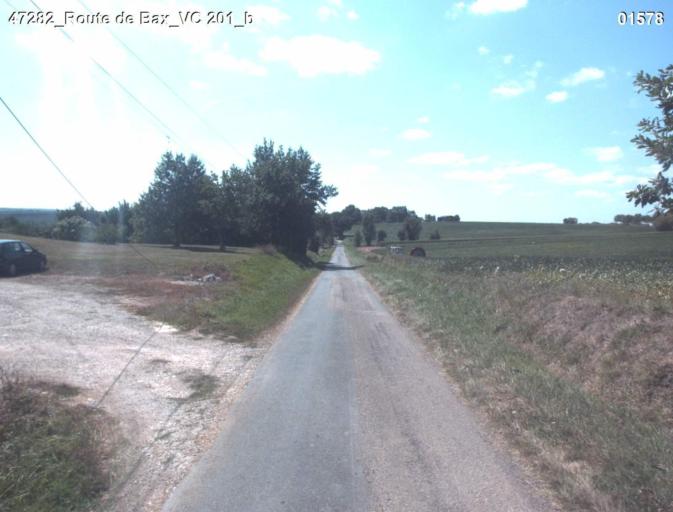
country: FR
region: Aquitaine
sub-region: Departement du Lot-et-Garonne
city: Laplume
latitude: 44.0818
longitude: 0.4976
